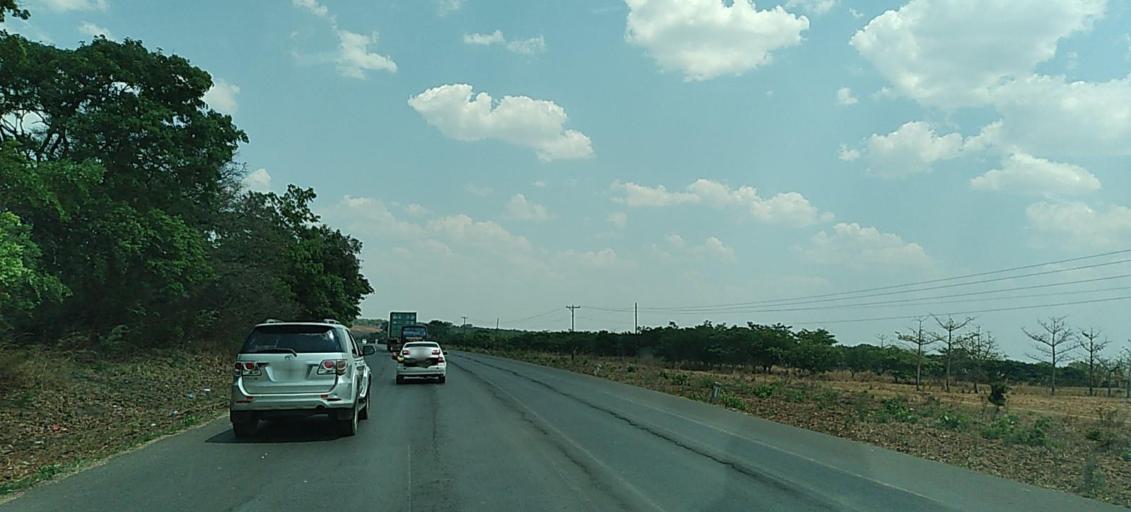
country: ZM
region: Central
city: Kabwe
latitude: -14.3103
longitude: 28.5450
